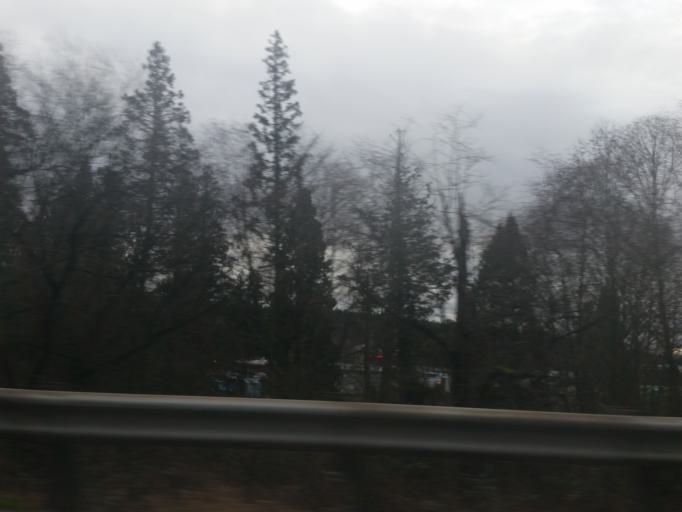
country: US
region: Washington
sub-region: King County
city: Woodinville
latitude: 47.7605
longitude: -122.1594
